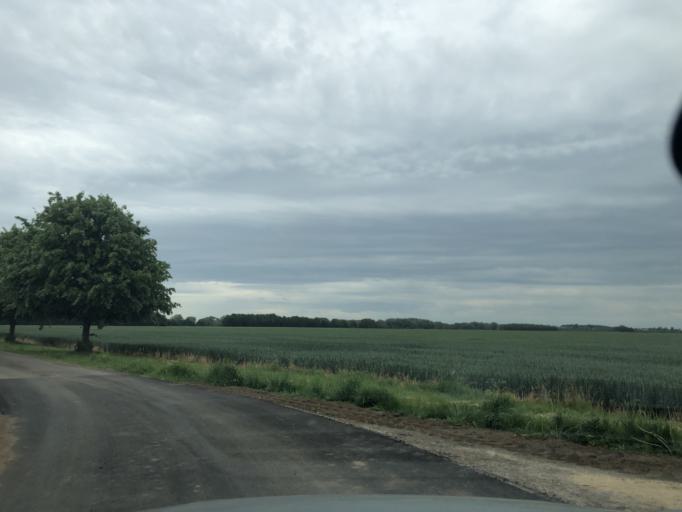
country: GB
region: England
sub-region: North Yorkshire
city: Thirsk
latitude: 54.2008
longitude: -1.3589
